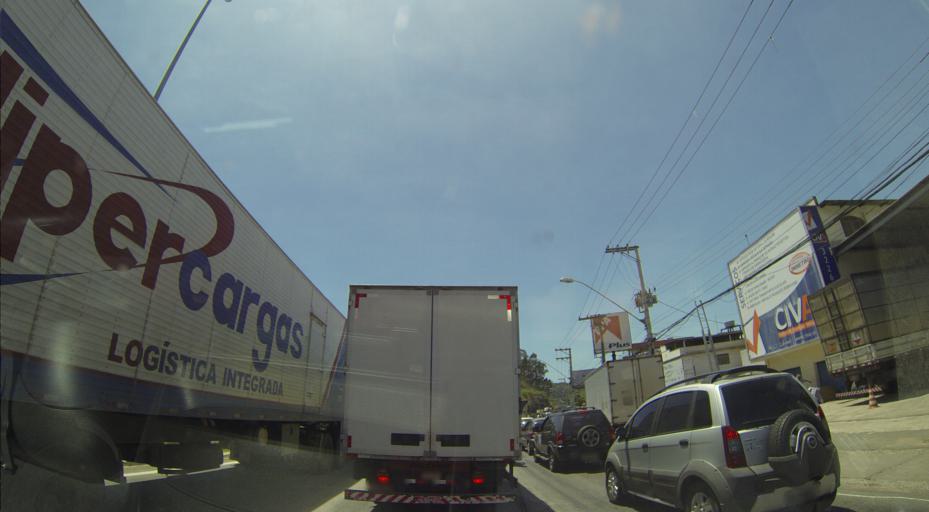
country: BR
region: Espirito Santo
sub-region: Vitoria
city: Vitoria
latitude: -20.3311
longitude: -40.3644
